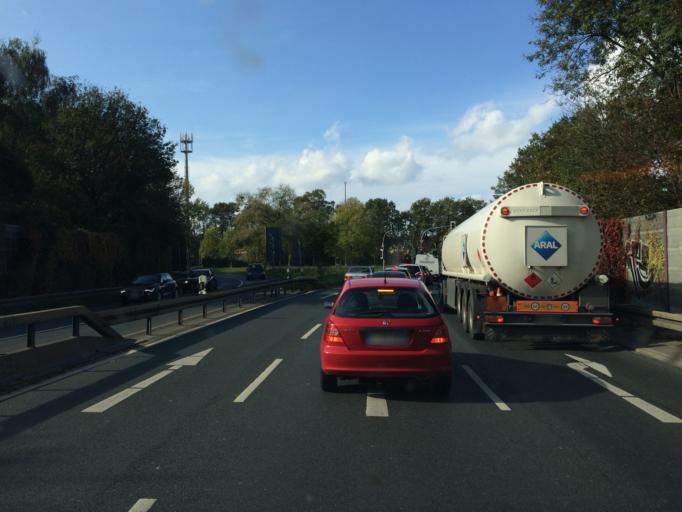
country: DE
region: Lower Saxony
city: Hemmingen
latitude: 52.3376
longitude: 9.7225
